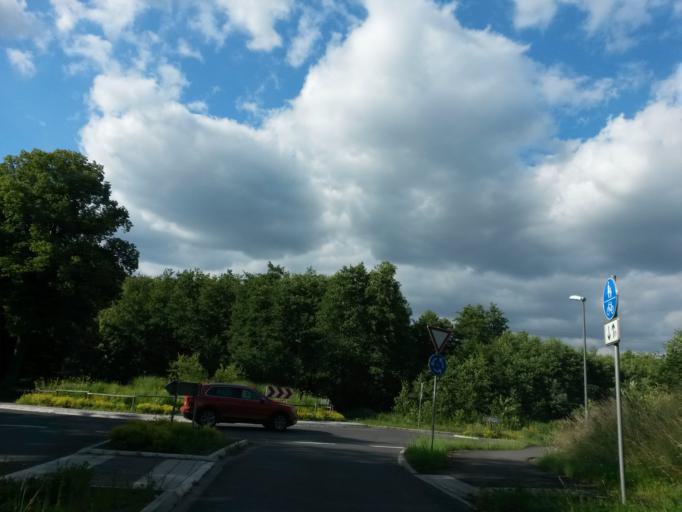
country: DE
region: North Rhine-Westphalia
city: Waldbrol
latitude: 50.8929
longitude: 7.6334
